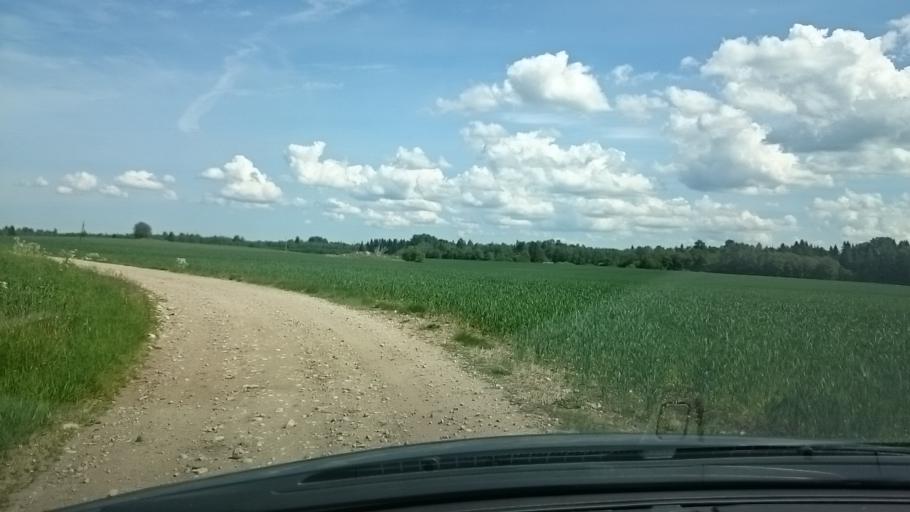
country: EE
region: Harju
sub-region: Anija vald
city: Kehra
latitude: 59.0897
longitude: 25.2911
